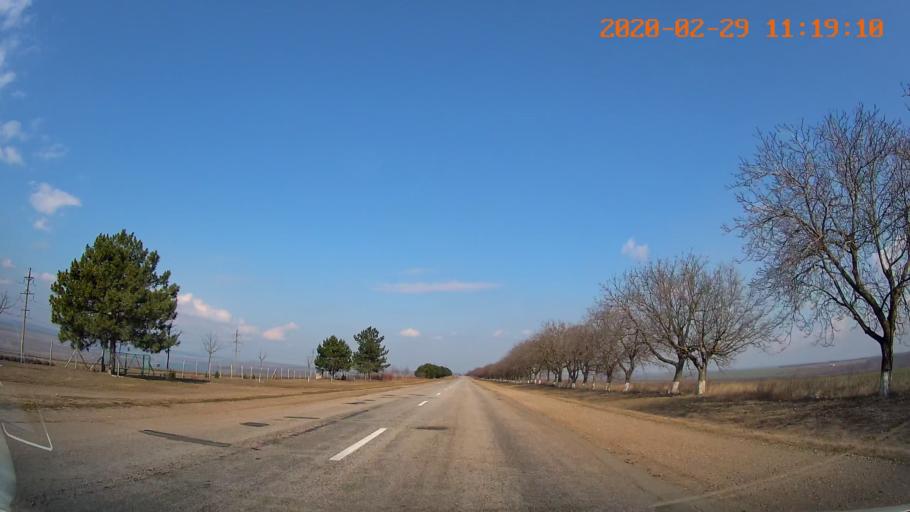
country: MD
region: Telenesti
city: Cocieri
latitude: 47.3458
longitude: 29.1755
